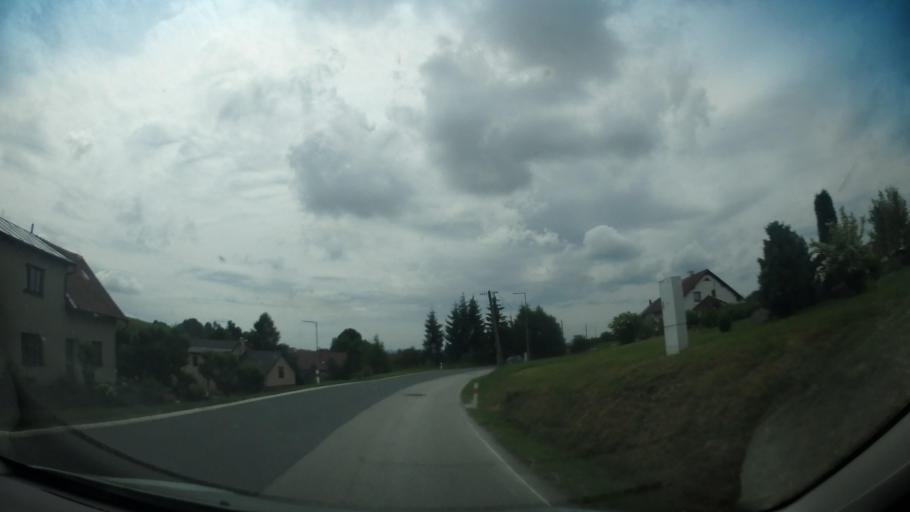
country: CZ
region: Vysocina
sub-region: Okres Zd'ar nad Sazavou
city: Nove Mesto na Morave
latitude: 49.5830
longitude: 16.0797
